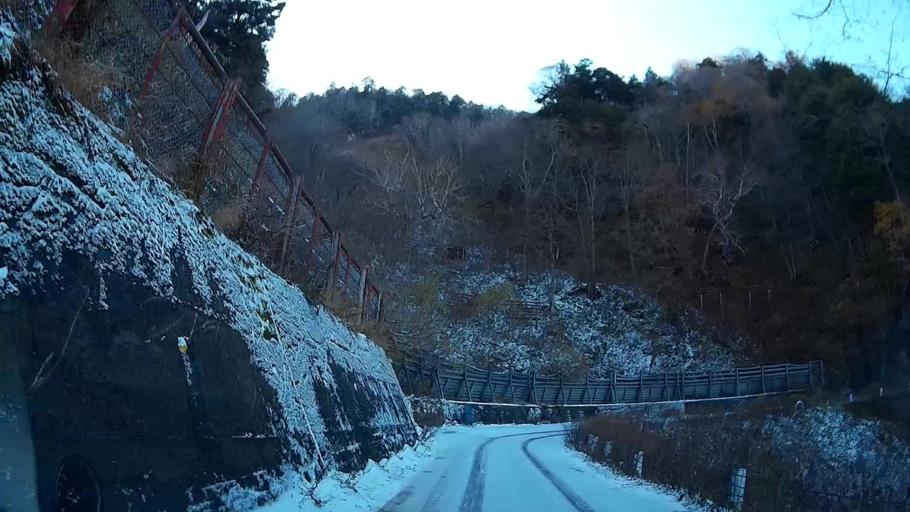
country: JP
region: Nagano
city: Hotaka
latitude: 36.2033
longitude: 137.5982
